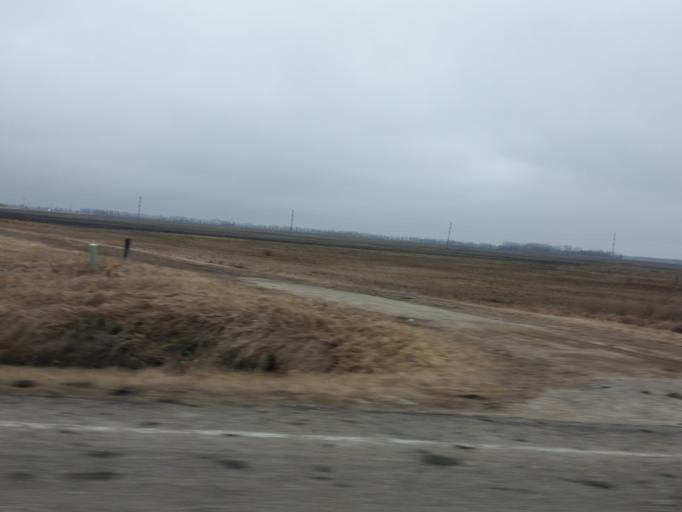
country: US
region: North Dakota
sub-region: Walsh County
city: Grafton
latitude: 48.3532
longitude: -97.1864
